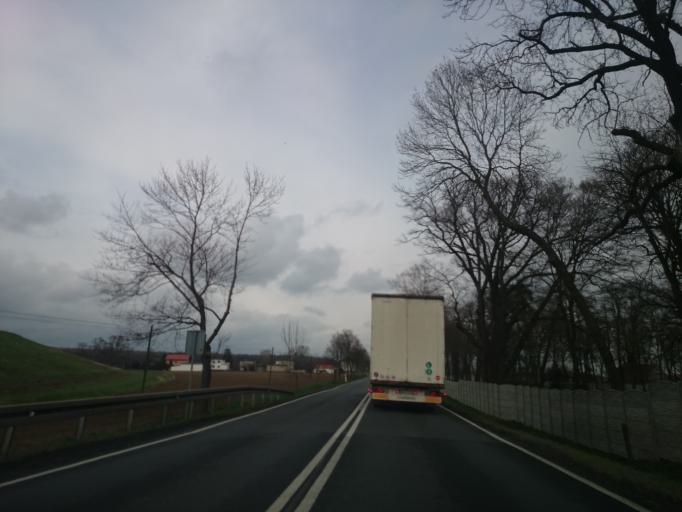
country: PL
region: Opole Voivodeship
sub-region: Powiat nyski
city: Otmuchow
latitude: 50.4516
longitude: 17.1455
